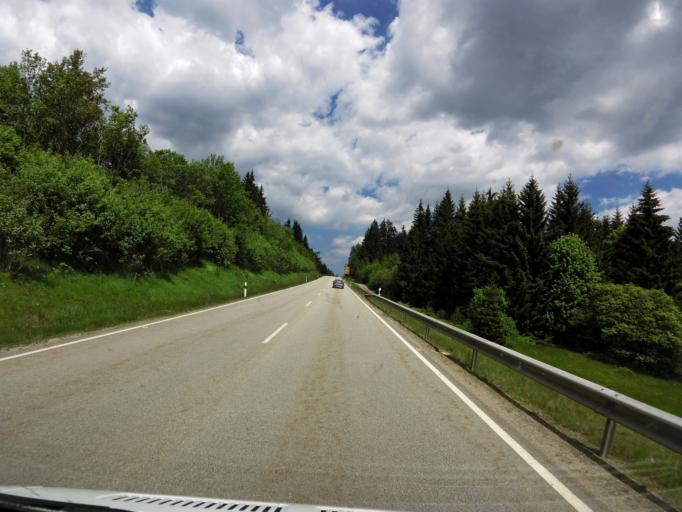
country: DE
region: Bavaria
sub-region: Lower Bavaria
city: Philippsreut
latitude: 48.8667
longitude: 13.6832
